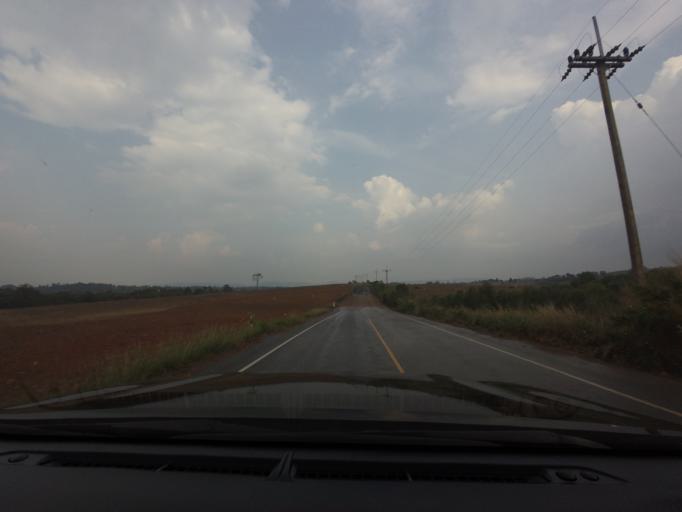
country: TH
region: Nakhon Ratchasima
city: Wang Nam Khiao
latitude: 14.4141
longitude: 101.7559
